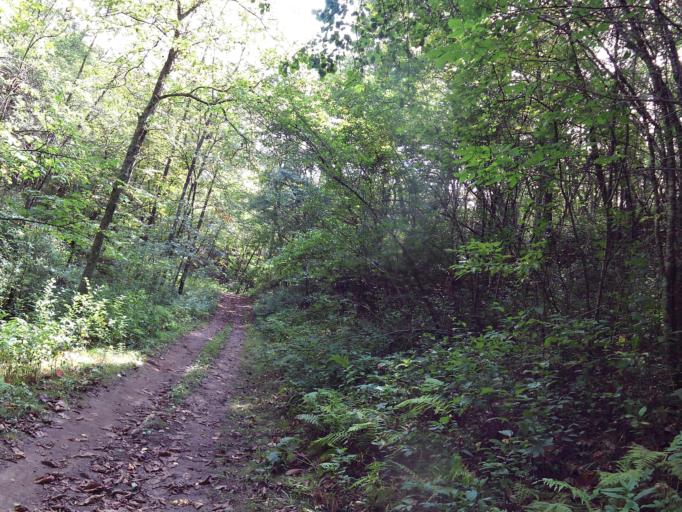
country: US
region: Minnesota
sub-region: Washington County
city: Afton
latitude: 44.8668
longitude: -92.7959
